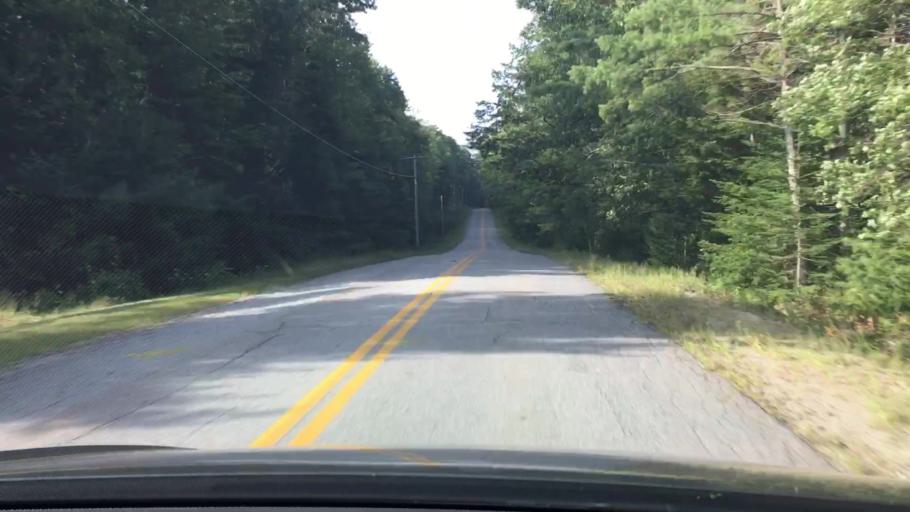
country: US
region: Maine
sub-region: Hancock County
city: Orland
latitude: 44.5258
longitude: -68.7638
